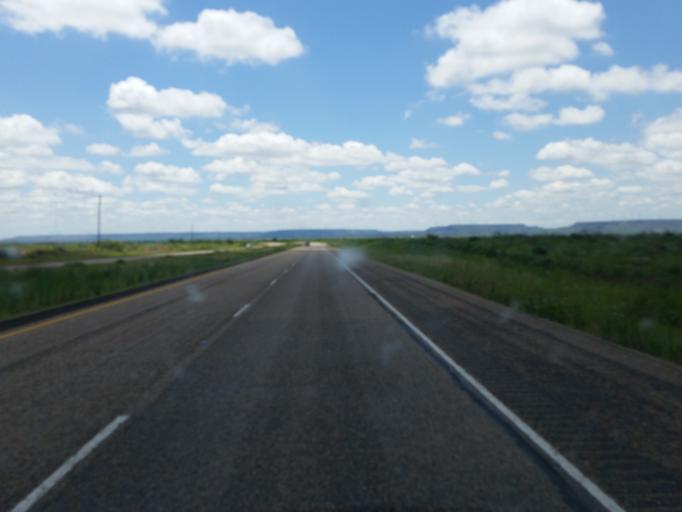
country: US
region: Texas
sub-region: Garza County
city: Post
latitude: 33.0795
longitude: -101.2396
